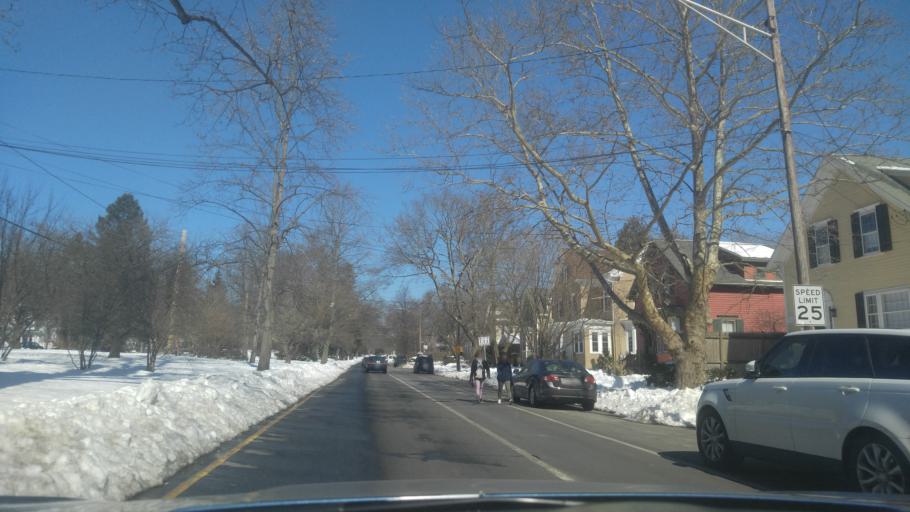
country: US
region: Rhode Island
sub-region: Providence County
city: East Providence
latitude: 41.8344
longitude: -71.3839
